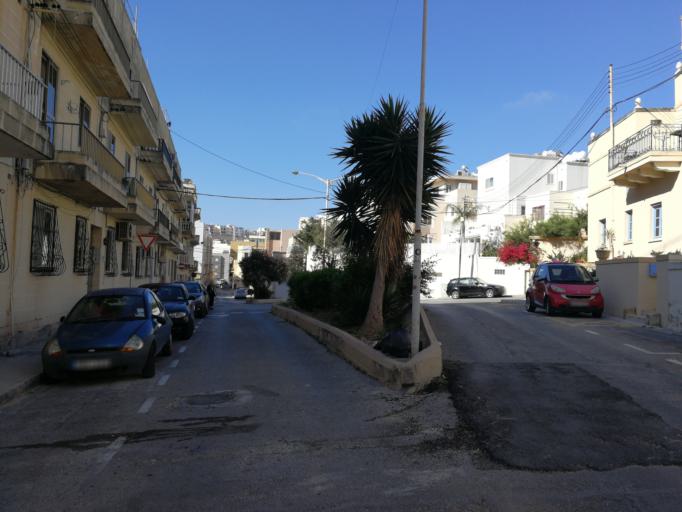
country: MT
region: Saint Julian
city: San Giljan
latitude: 35.9197
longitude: 14.4888
